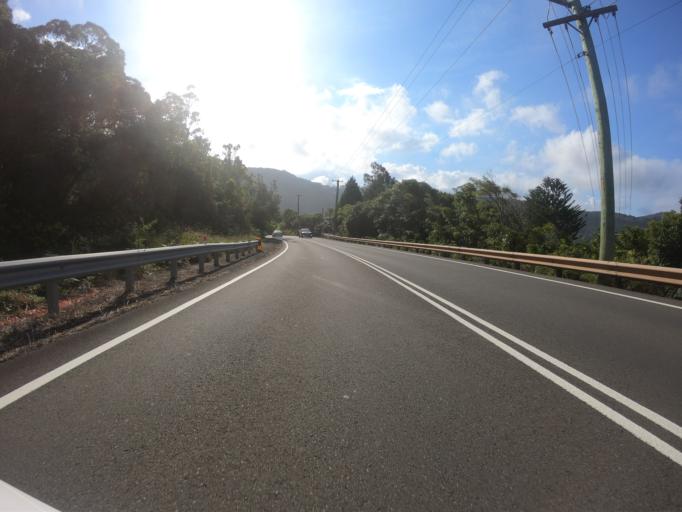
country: AU
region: New South Wales
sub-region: Wollongong
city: Helensburgh
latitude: -34.2342
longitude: 150.9854
